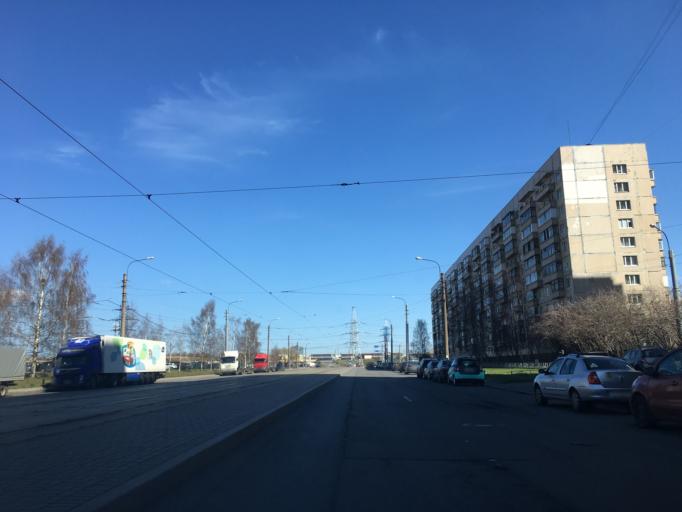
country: RU
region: St.-Petersburg
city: Uritsk
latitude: 59.8575
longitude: 30.2040
